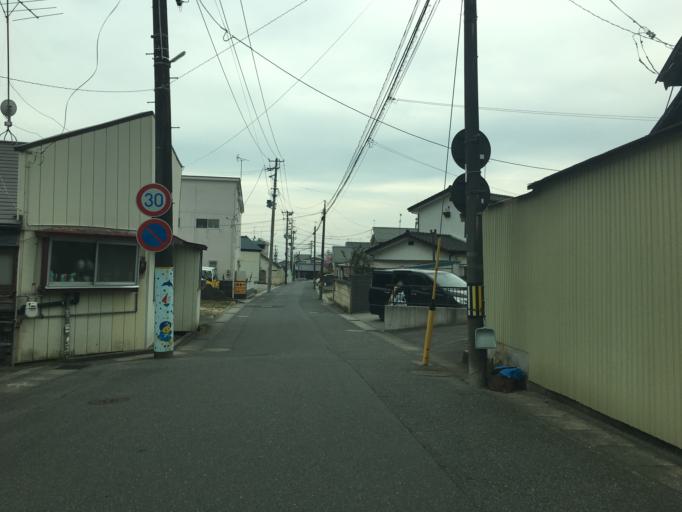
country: JP
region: Fukushima
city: Iwaki
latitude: 36.9522
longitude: 140.9114
